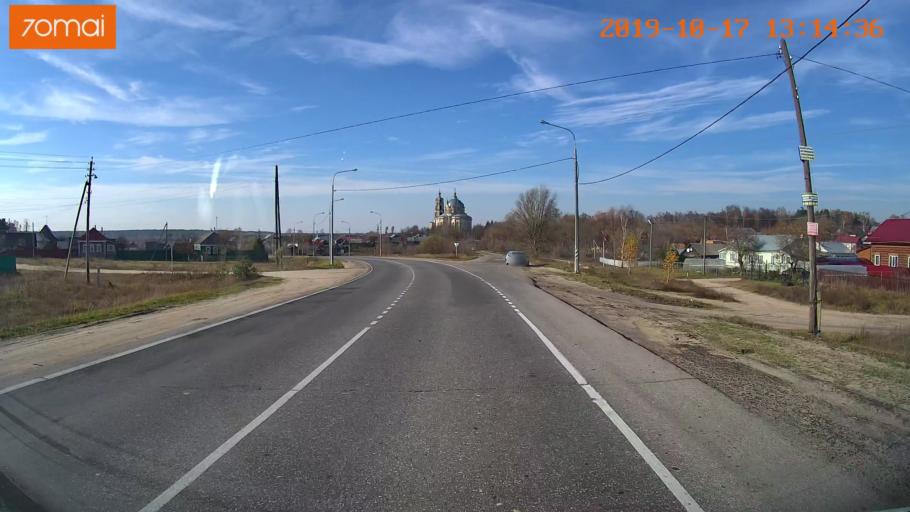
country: RU
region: Rjazan
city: Gus'-Zheleznyy
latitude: 55.0532
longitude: 41.1685
